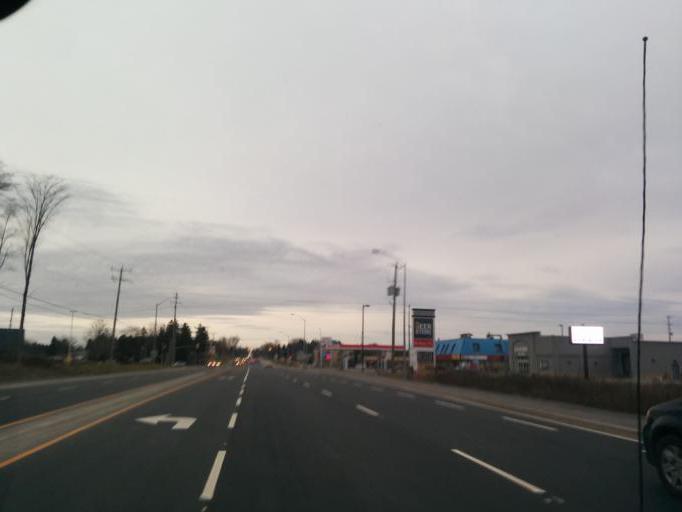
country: CA
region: Ontario
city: Shelburne
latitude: 44.0821
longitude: -80.1858
